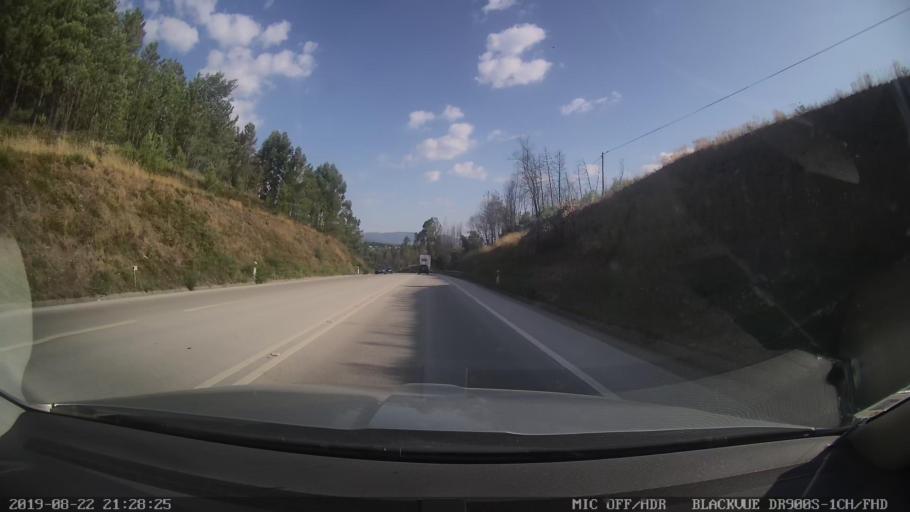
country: PT
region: Leiria
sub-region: Pedrogao Grande
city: Pedrogao Grande
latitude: 39.8923
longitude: -8.1212
